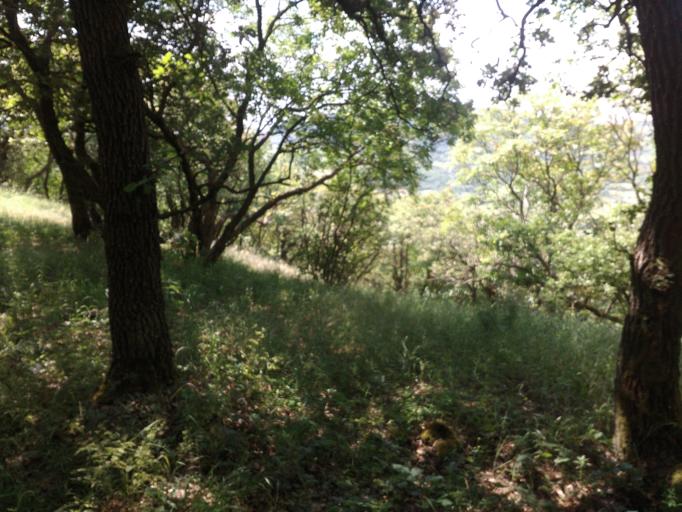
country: HU
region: Komarom-Esztergom
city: Esztergom
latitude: 47.8086
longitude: 18.7973
